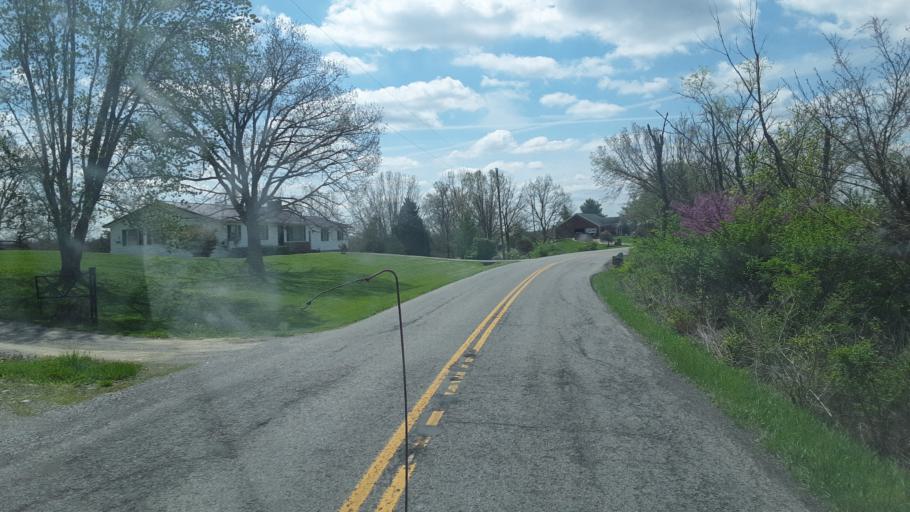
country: US
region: Kentucky
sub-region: Grant County
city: Dry Ridge
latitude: 38.6537
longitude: -84.7027
